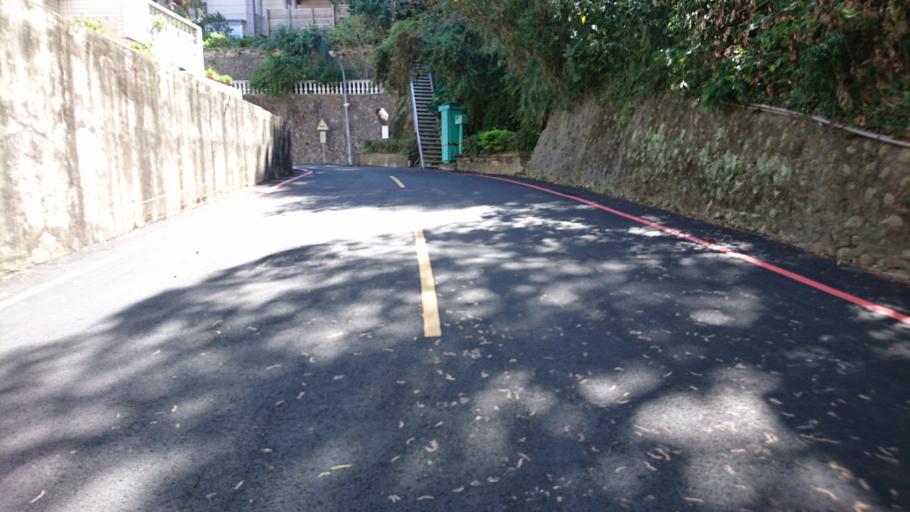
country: TW
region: Taiwan
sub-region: Hsinchu
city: Zhubei
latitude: 24.7888
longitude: 121.0744
